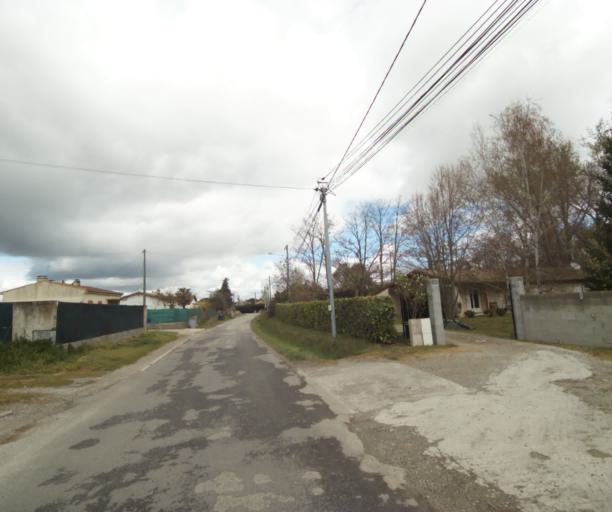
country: FR
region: Midi-Pyrenees
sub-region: Departement de l'Ariege
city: Saverdun
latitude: 43.2215
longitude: 1.5722
